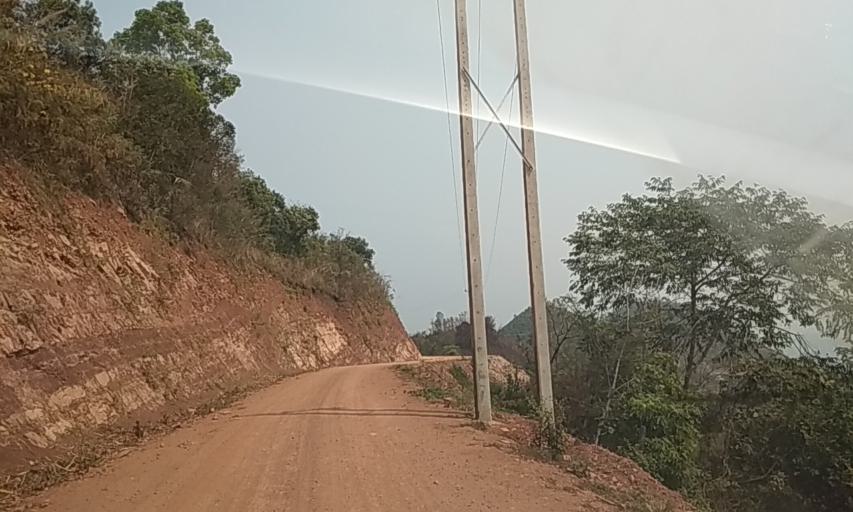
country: VN
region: Huyen Dien Bien
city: Dien Bien Phu
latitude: 21.5032
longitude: 102.7924
